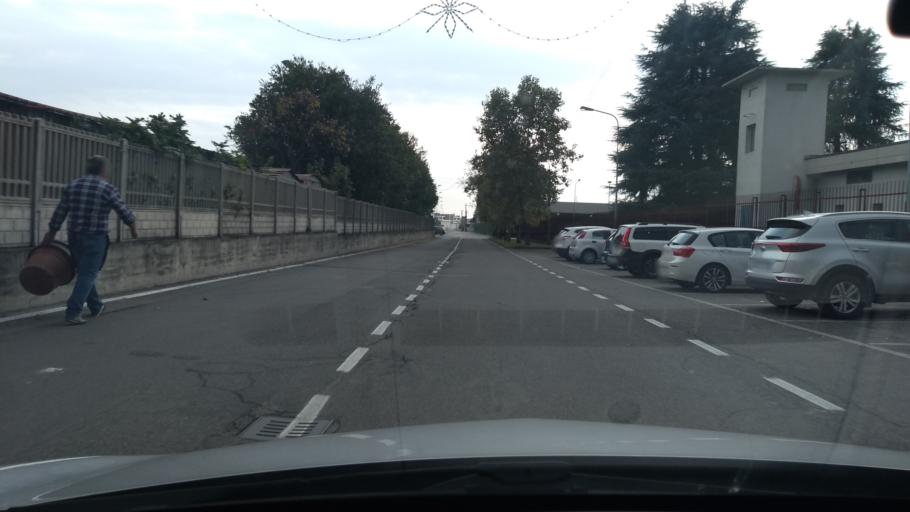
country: IT
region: Lombardy
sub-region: Provincia di Bergamo
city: Verdellino
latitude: 45.6014
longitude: 9.6135
